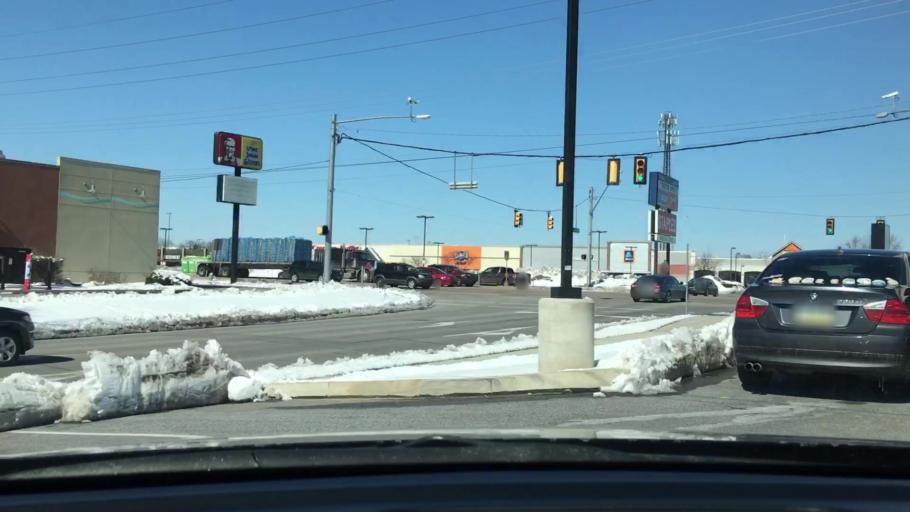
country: US
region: Pennsylvania
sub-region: York County
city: North York
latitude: 39.9796
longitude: -76.7520
